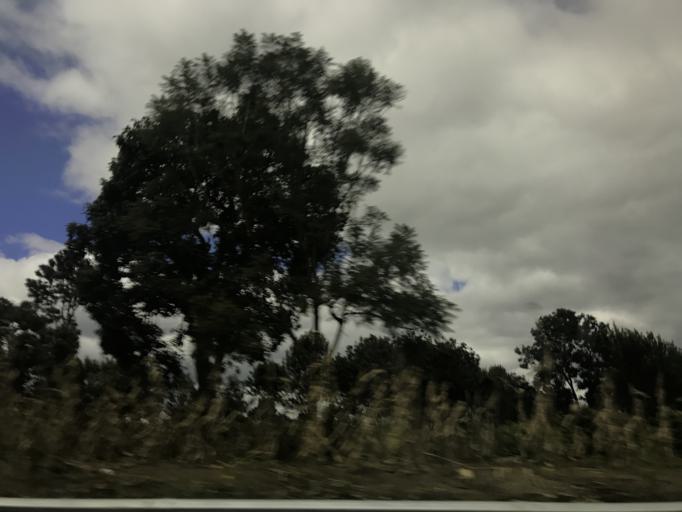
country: GT
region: Chimaltenango
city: El Tejar
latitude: 14.6280
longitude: -90.7963
